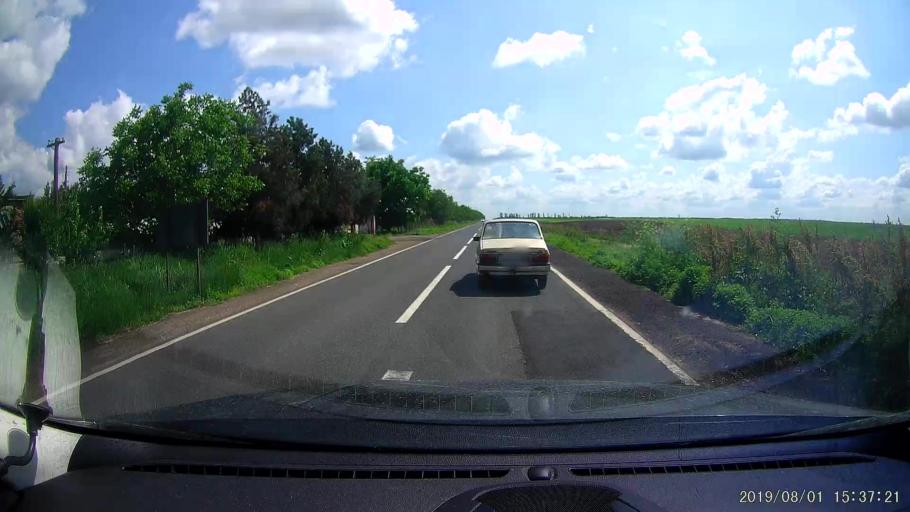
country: RO
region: Braila
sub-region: Comuna Insuratei
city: Insuratei
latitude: 44.9032
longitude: 27.5892
